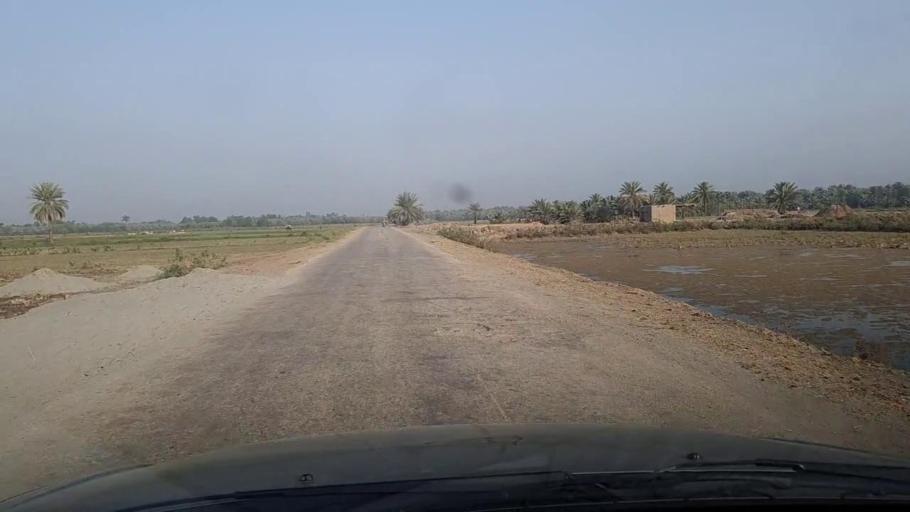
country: PK
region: Sindh
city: Khairpur
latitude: 27.5503
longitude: 68.6917
